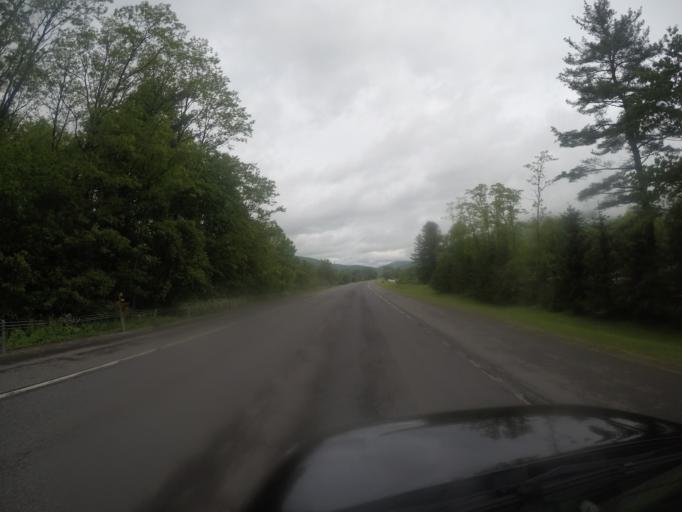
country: US
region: New York
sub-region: Ulster County
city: Shokan
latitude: 42.0432
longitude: -74.2828
